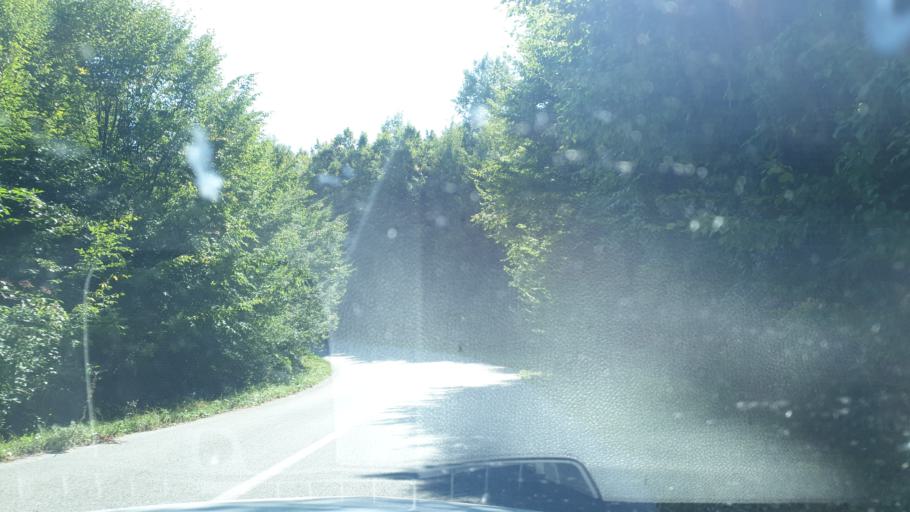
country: RS
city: Zlatibor
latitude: 43.6595
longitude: 19.8303
